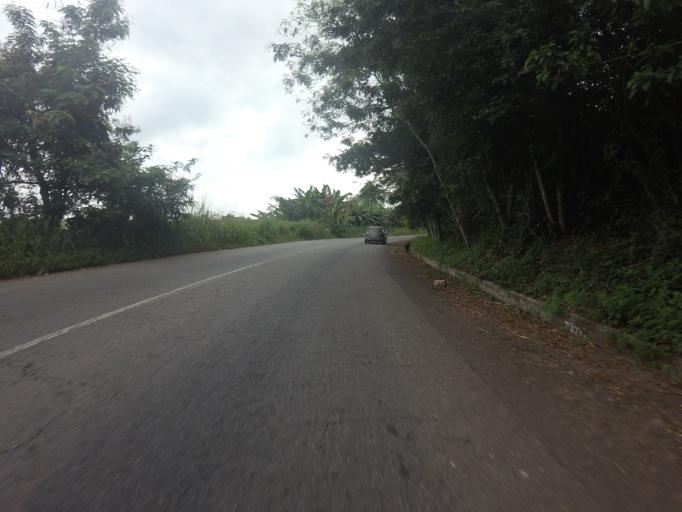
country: GH
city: Akropong
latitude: 5.9630
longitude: -0.1149
